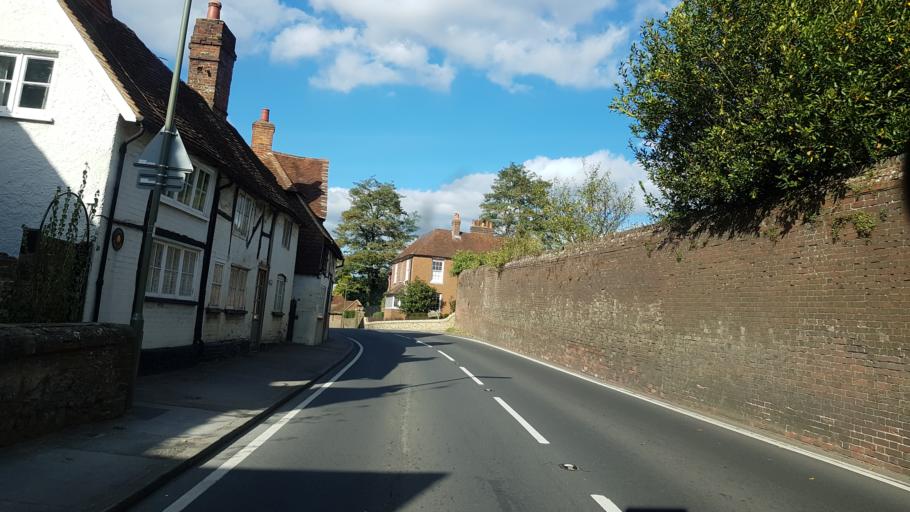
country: GB
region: England
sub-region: Surrey
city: Milford
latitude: 51.1494
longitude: -0.6467
